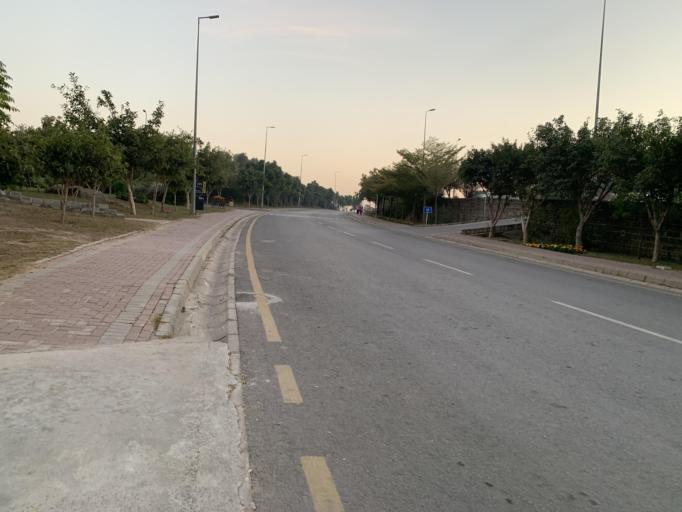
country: PK
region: Punjab
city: Rawalpindi
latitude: 33.6439
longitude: 72.9942
